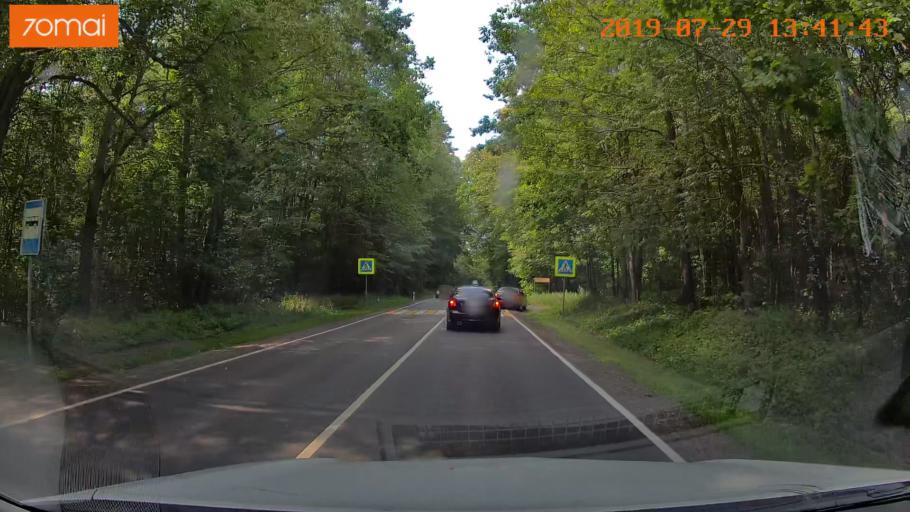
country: RU
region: Kaliningrad
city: Svetlyy
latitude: 54.7359
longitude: 20.1225
